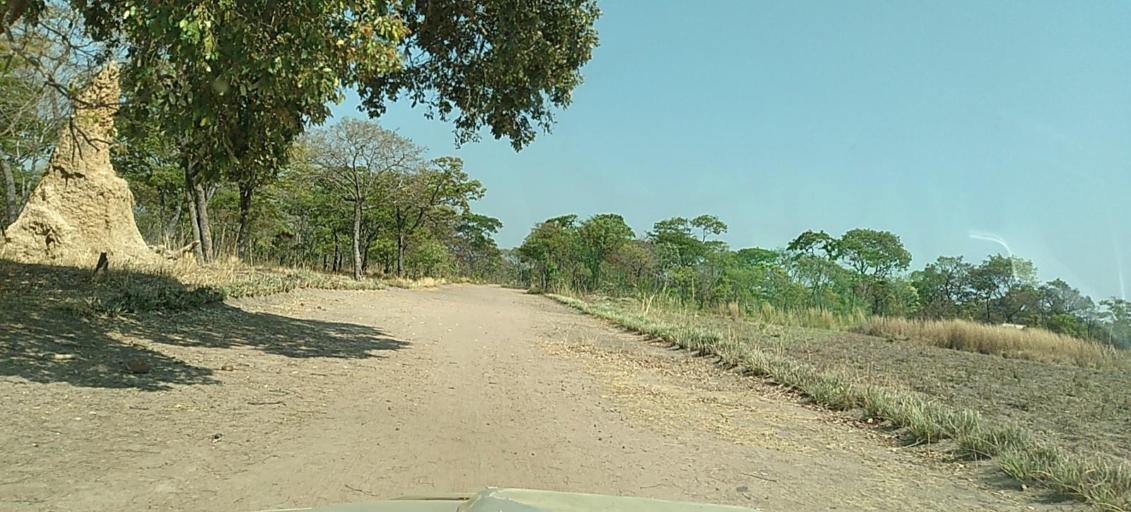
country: ZM
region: North-Western
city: Kalengwa
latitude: -13.3082
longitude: 24.8066
